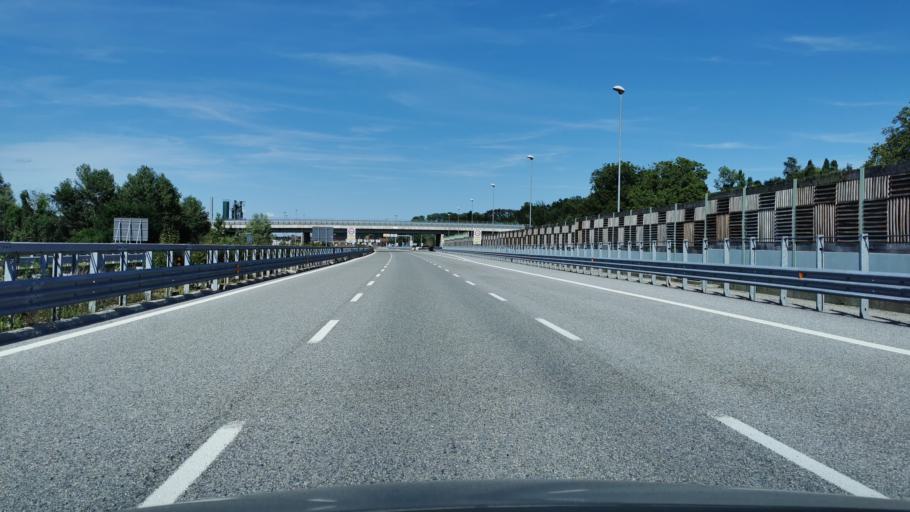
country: IT
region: Piedmont
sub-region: Provincia di Cuneo
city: Castelletto Stura
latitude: 44.4278
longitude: 7.6011
